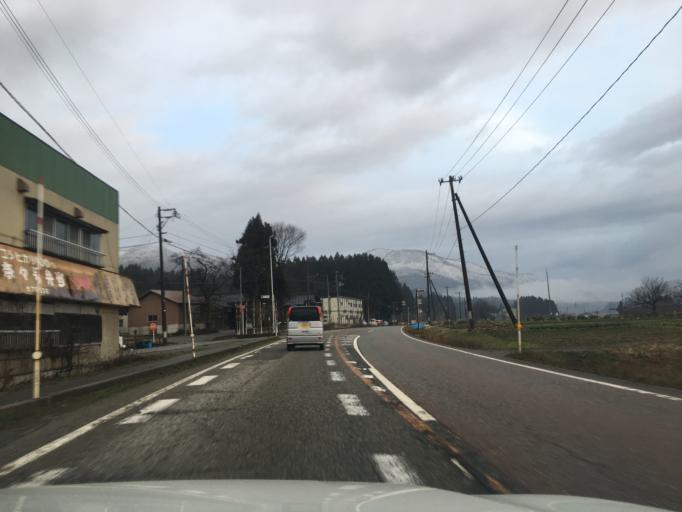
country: JP
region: Niigata
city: Murakami
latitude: 38.3353
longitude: 139.5525
